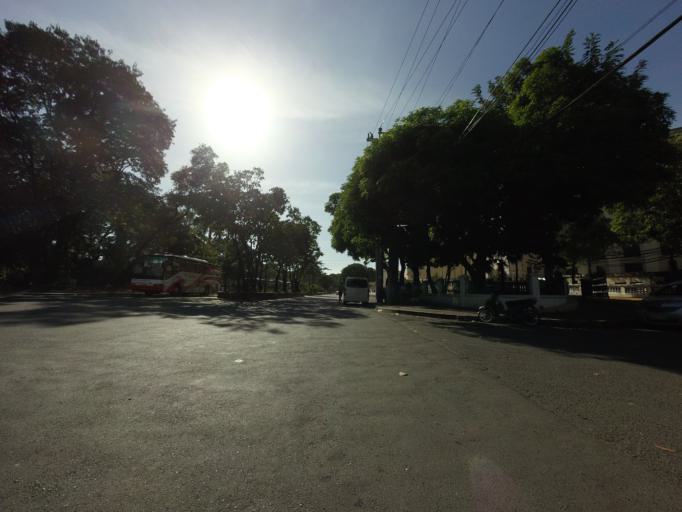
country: PH
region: Metro Manila
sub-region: City of Manila
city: Quiapo
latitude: 14.5953
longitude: 120.9799
